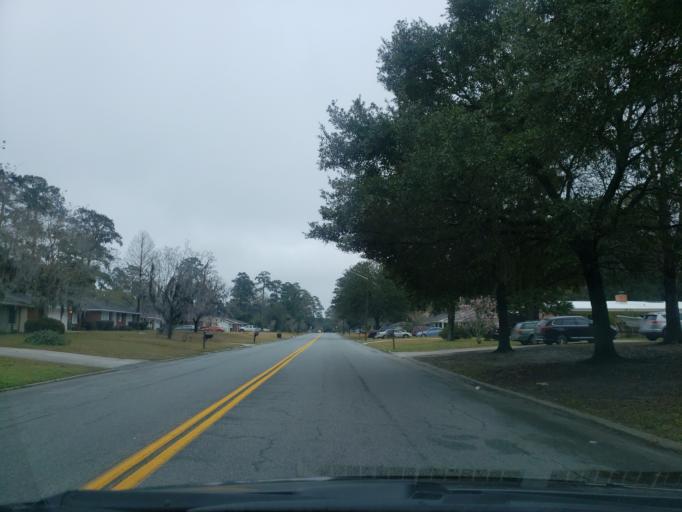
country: US
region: Georgia
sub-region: Chatham County
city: Montgomery
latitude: 31.9732
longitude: -81.1571
